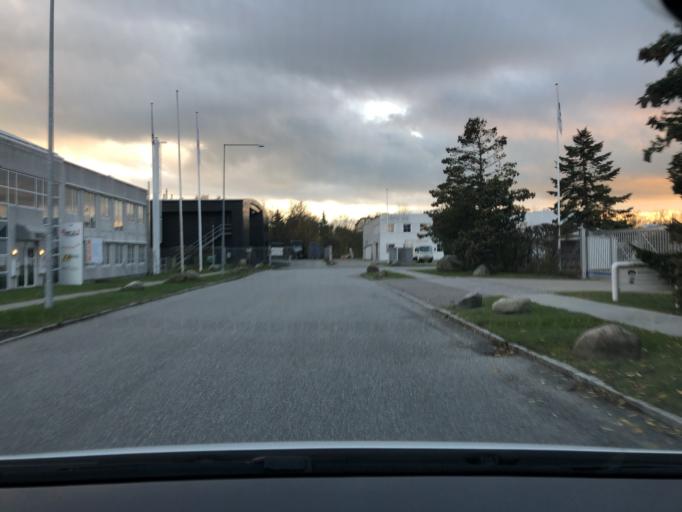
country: DK
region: Capital Region
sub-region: Tarnby Kommune
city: Tarnby
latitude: 55.6151
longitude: 12.6218
